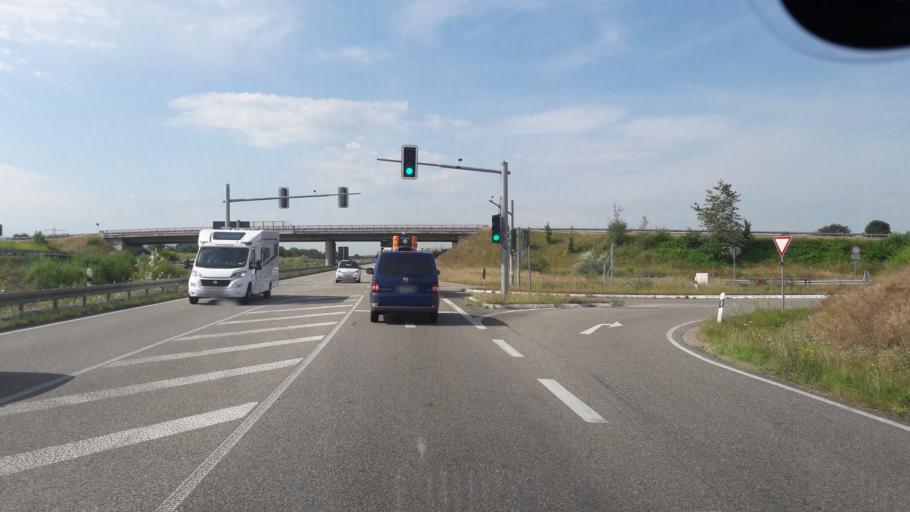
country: DE
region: Baden-Wuerttemberg
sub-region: Karlsruhe Region
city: Bietigheim
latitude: 48.9010
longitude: 8.2582
